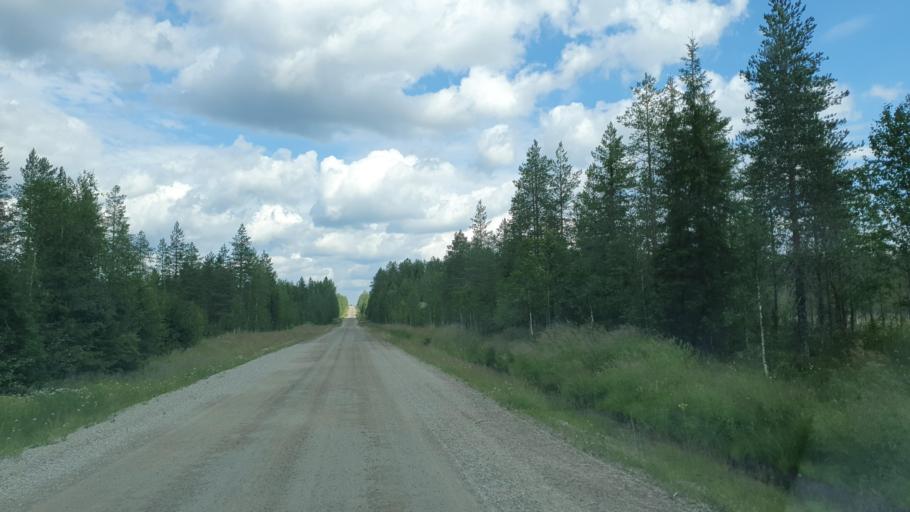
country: FI
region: Kainuu
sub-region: Kehys-Kainuu
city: Kuhmo
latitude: 64.4682
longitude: 29.5978
